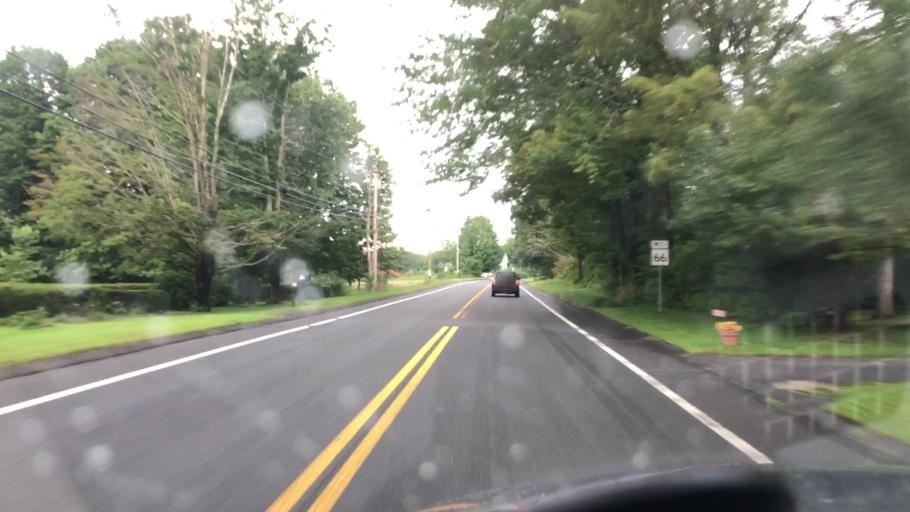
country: US
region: Massachusetts
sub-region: Hampshire County
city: Westhampton
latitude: 42.2896
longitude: -72.7415
